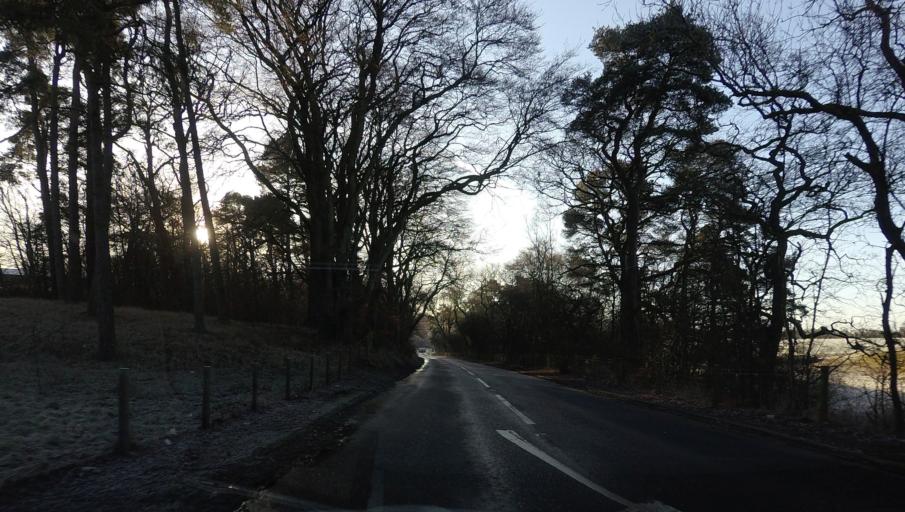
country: GB
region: Scotland
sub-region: North Lanarkshire
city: Newmains
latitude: 55.7997
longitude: -3.8499
